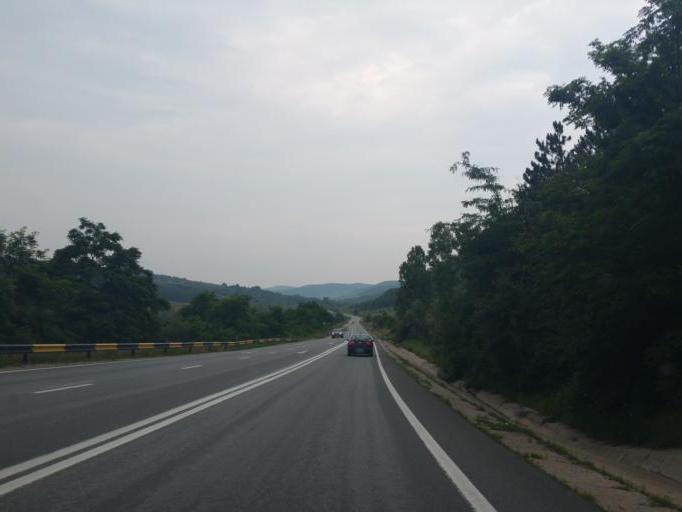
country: RO
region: Salaj
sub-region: Comuna Dragu
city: Dragu
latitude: 46.9462
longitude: 23.3695
